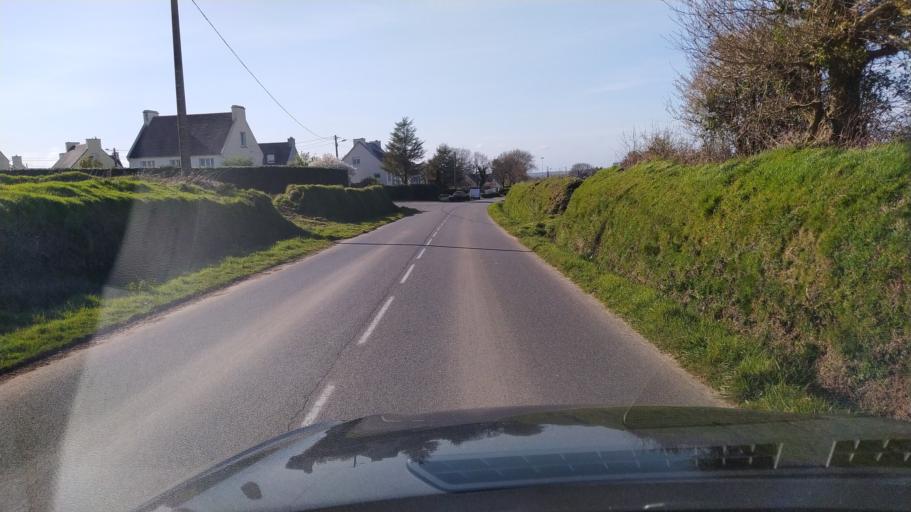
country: FR
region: Brittany
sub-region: Departement du Finistere
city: Lampaul-Guimiliau
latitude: 48.4844
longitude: -4.0326
